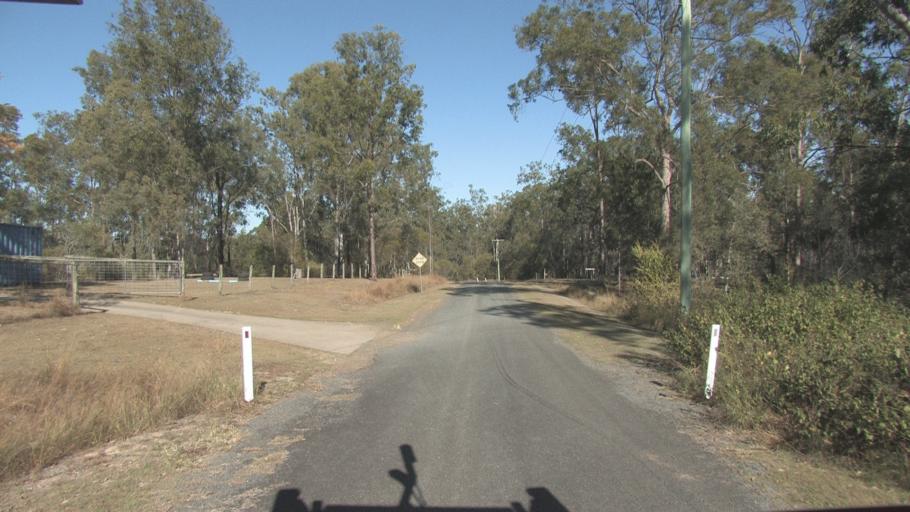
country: AU
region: Queensland
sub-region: Logan
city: Cedar Vale
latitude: -27.8467
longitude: 153.0579
